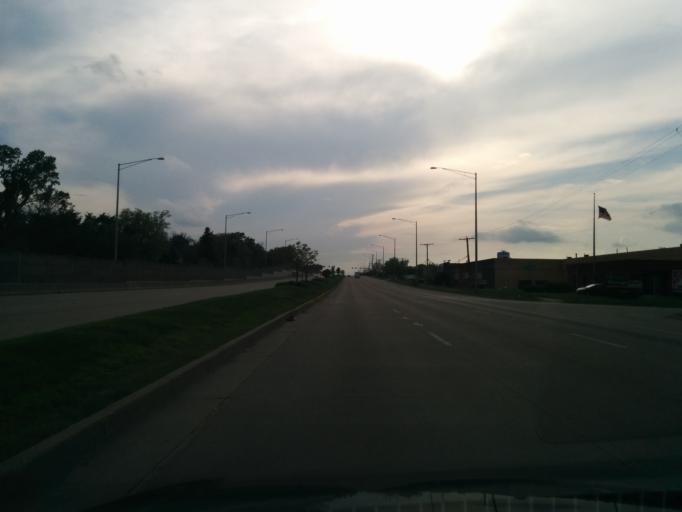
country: US
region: Illinois
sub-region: DuPage County
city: Lombard
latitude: 41.9048
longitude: -88.0191
